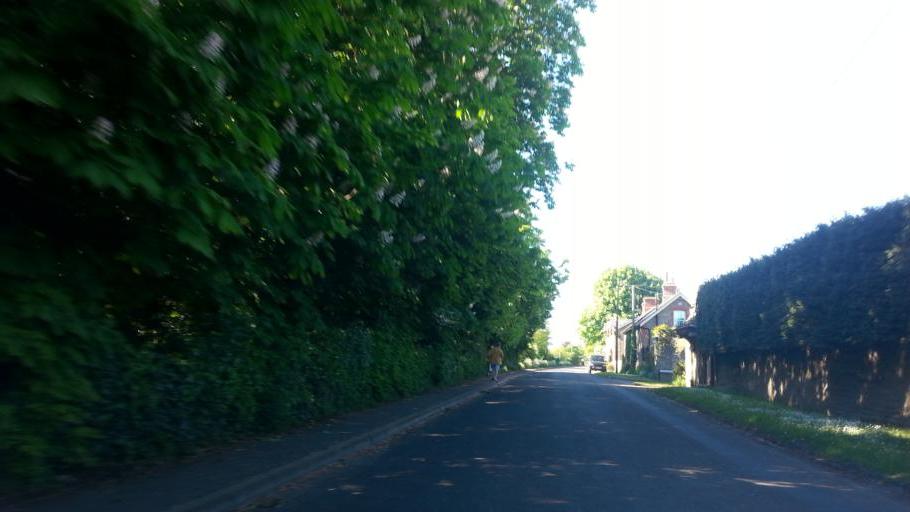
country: GB
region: England
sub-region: Somerset
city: Milborne Port
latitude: 50.9697
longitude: -2.4619
